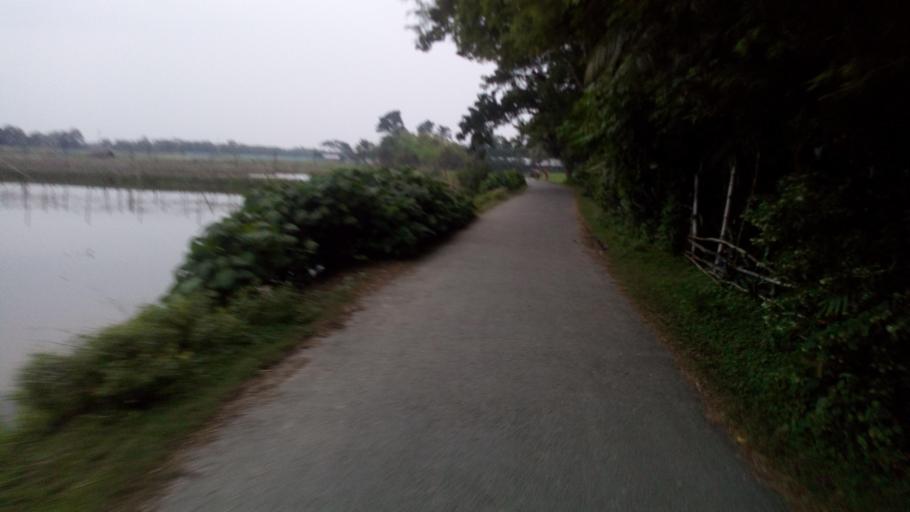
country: BD
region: Khulna
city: Phultala
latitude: 22.7634
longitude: 89.4072
